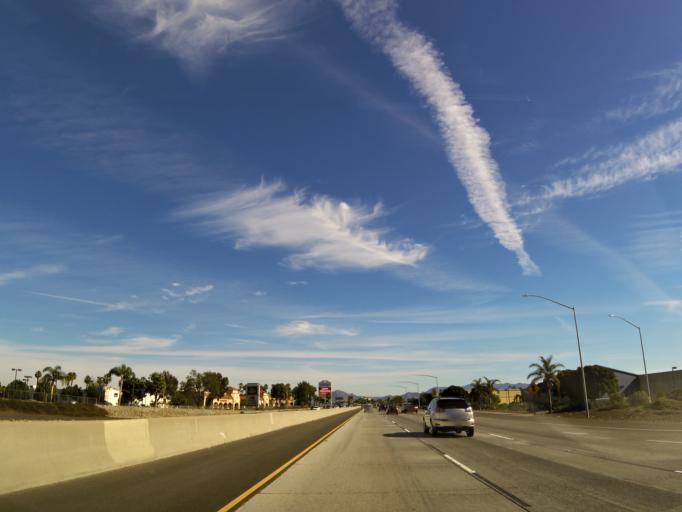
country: US
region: California
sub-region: Ventura County
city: El Rio
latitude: 34.2249
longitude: -119.1581
